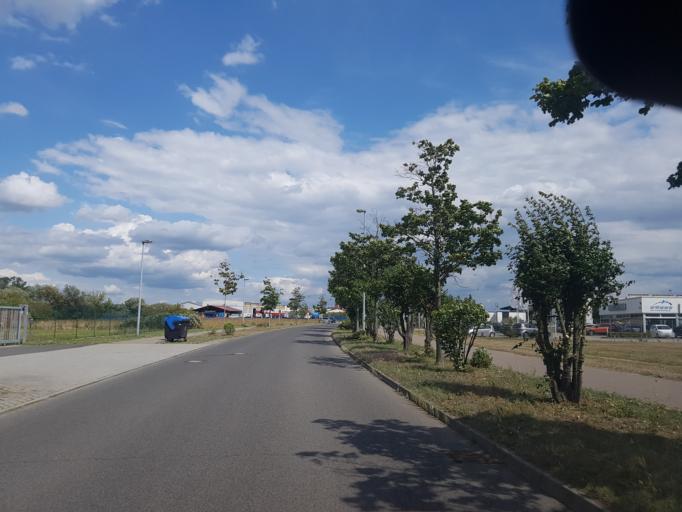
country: DE
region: Brandenburg
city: Herzberg
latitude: 51.6771
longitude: 13.2254
